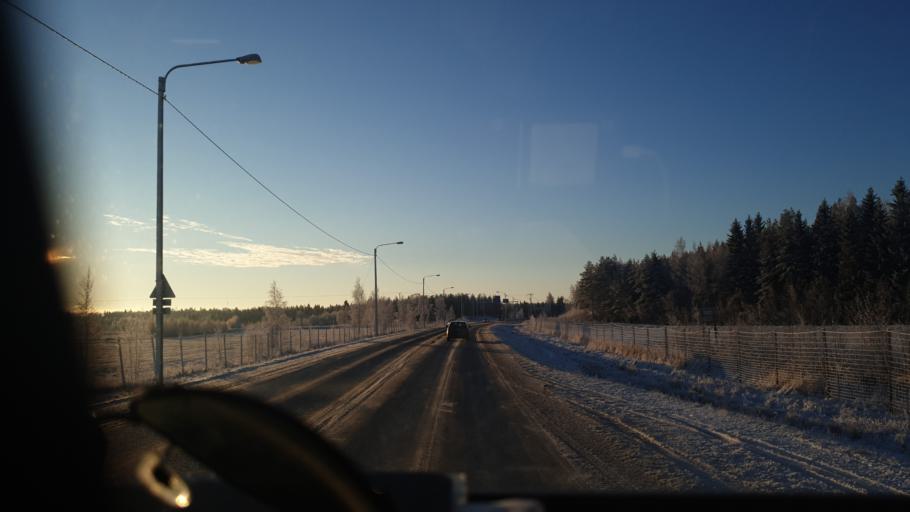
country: FI
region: Central Ostrobothnia
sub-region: Kokkola
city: Kaelviae
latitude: 63.8688
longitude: 23.3447
